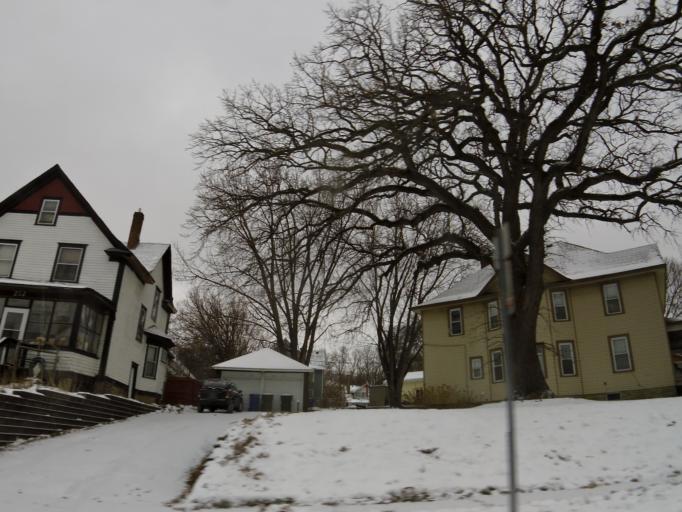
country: US
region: Minnesota
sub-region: Ramsey County
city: Saint Paul
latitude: 44.9323
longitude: -93.0965
